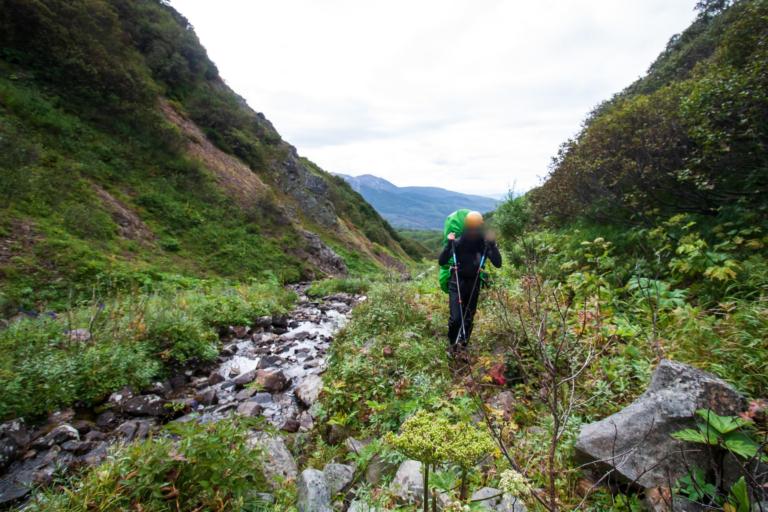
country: RU
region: Kamtsjatka
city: Yelizovo
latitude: 53.8262
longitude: 158.1455
